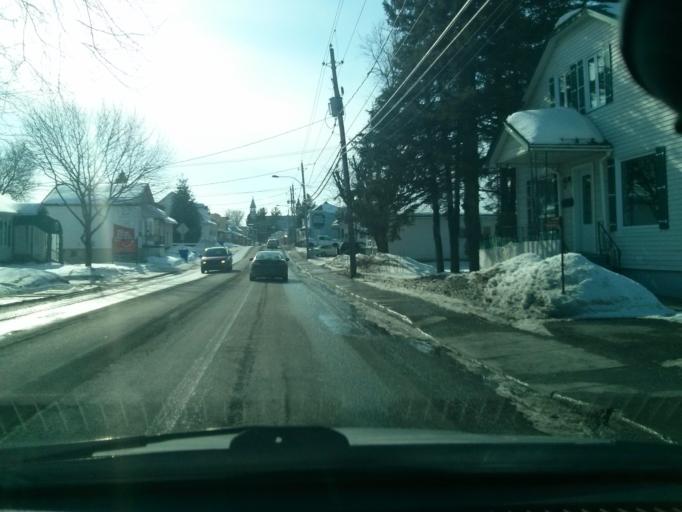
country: CA
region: Quebec
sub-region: Laurentides
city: Saint-Eustache
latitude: 45.6257
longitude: -73.9768
